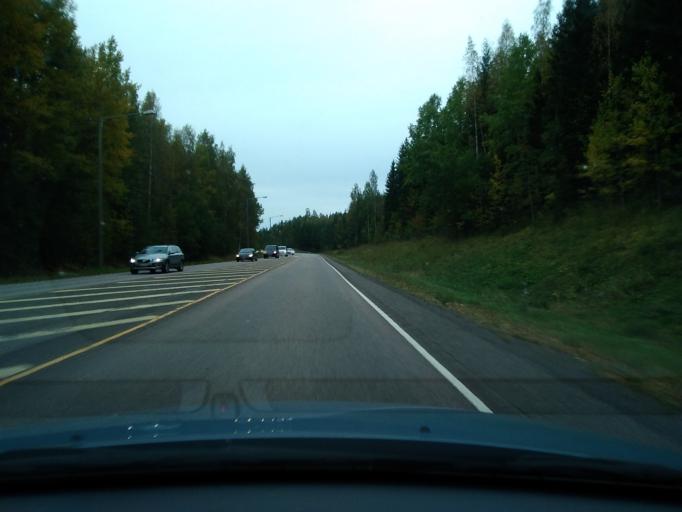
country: FI
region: Uusimaa
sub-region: Helsinki
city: Hyvinge
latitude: 60.5726
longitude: 24.8262
